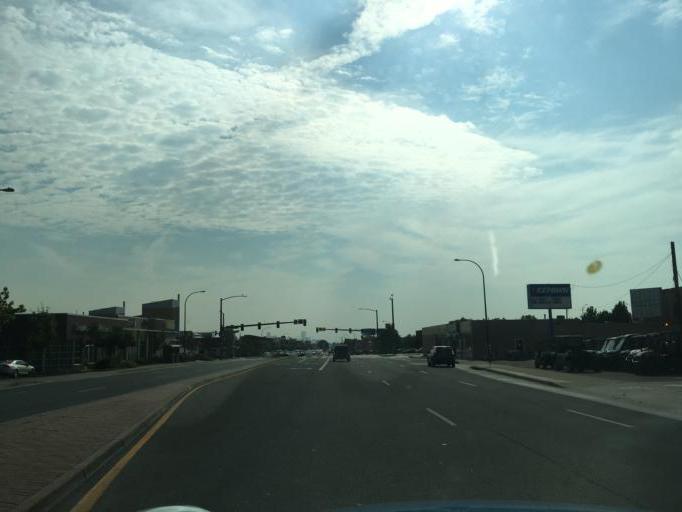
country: US
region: Colorado
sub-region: Jefferson County
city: Edgewater
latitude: 39.7402
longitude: -105.0833
